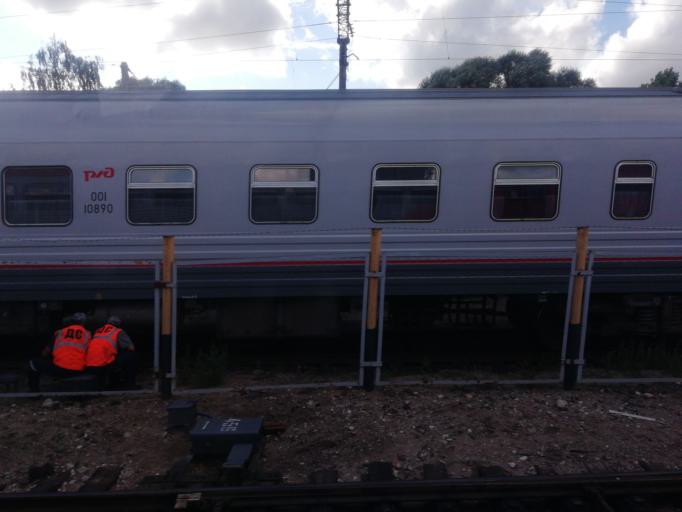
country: RU
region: Kaliningrad
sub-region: Gorod Kaliningrad
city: Kaliningrad
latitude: 54.6914
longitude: 20.4807
